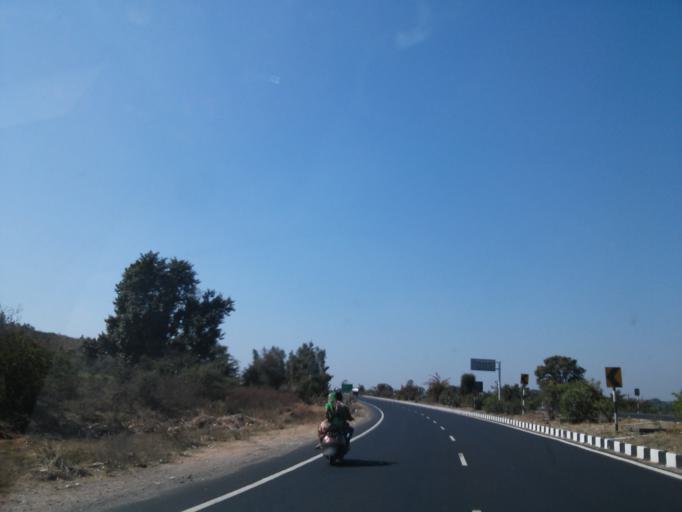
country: IN
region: Gujarat
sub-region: Sabar Kantha
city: Modasa
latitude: 23.6054
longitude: 73.1728
